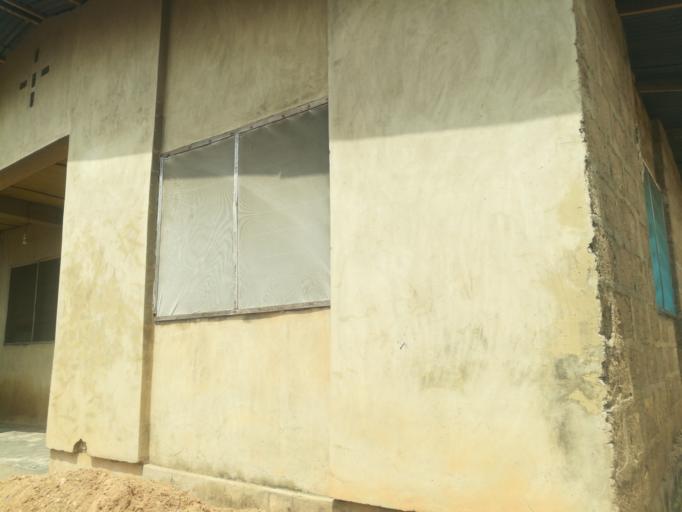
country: NG
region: Oyo
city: Ibadan
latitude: 7.4375
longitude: 3.9388
